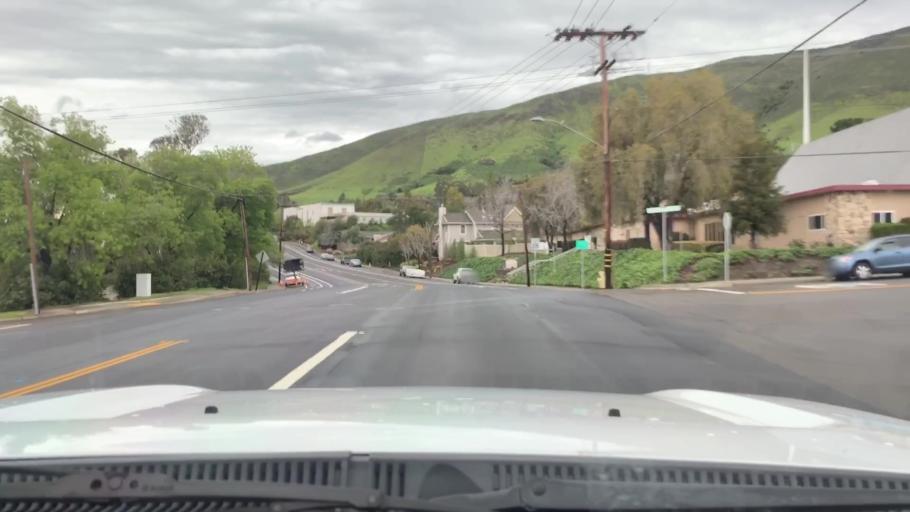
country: US
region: California
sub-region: San Luis Obispo County
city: San Luis Obispo
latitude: 35.2648
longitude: -120.6358
